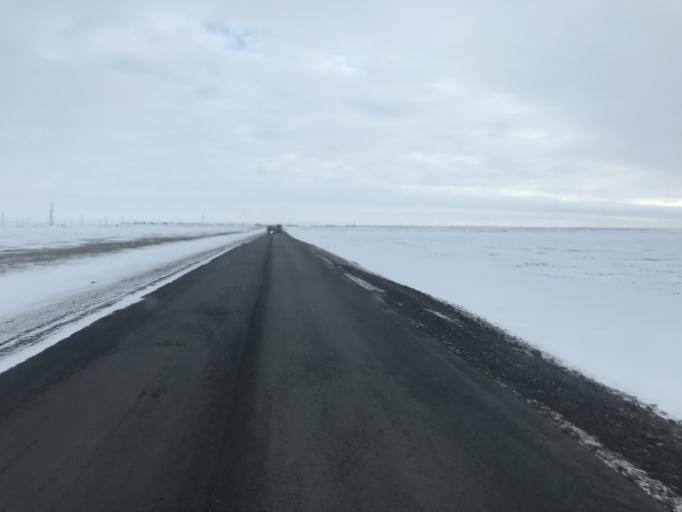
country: RU
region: Orenburg
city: Dombarovskiy
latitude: 49.9458
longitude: 60.1018
